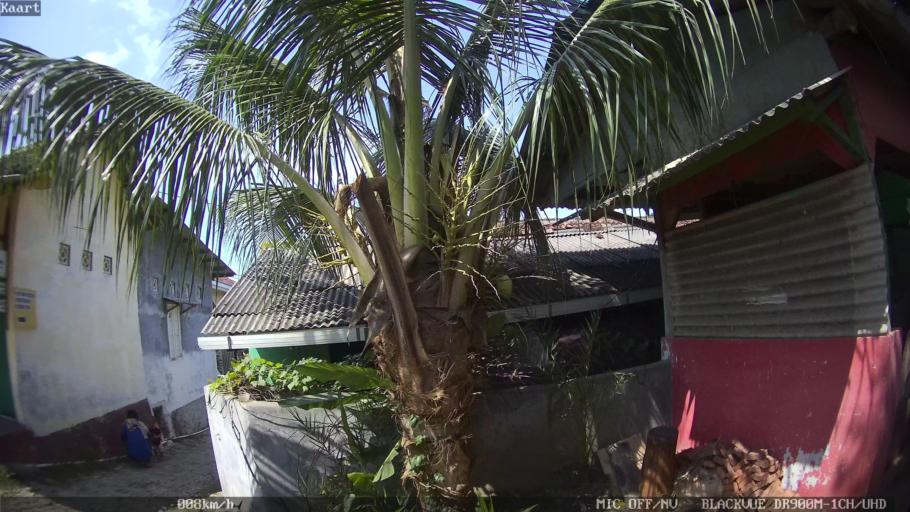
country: ID
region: Lampung
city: Kedaton
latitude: -5.3715
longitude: 105.2517
